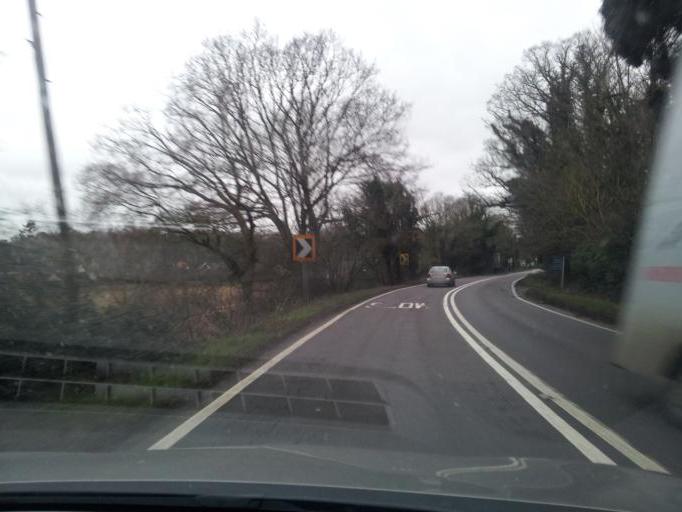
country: GB
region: England
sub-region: Suffolk
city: Great Barton
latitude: 52.2735
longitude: 0.7903
